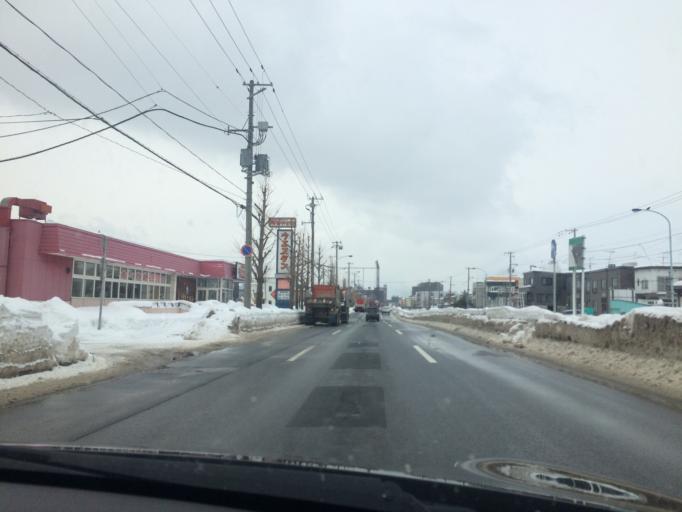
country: JP
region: Hokkaido
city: Sapporo
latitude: 43.0598
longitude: 141.4219
